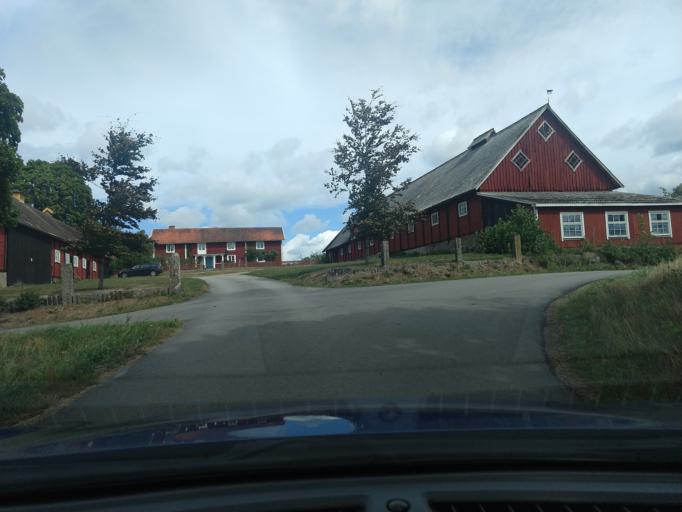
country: SE
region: Blekinge
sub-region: Ronneby Kommun
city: Brakne-Hoby
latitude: 56.2806
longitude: 15.1742
